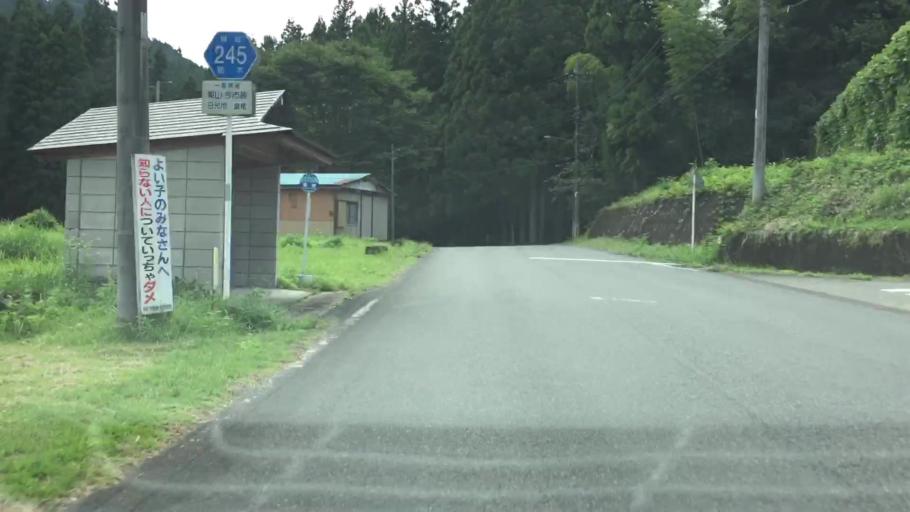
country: JP
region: Tochigi
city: Imaichi
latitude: 36.7589
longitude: 139.6831
